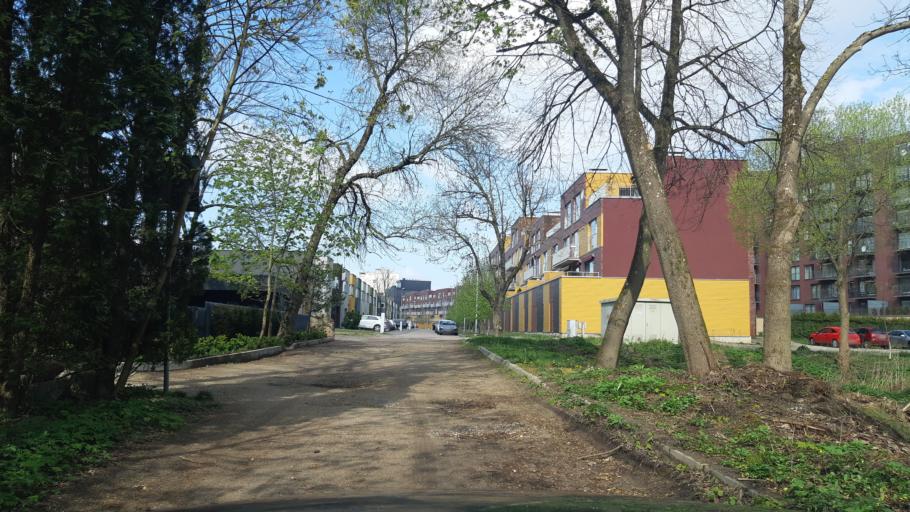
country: LT
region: Kauno apskritis
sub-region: Kaunas
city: Aleksotas
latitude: 54.8737
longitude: 23.9116
